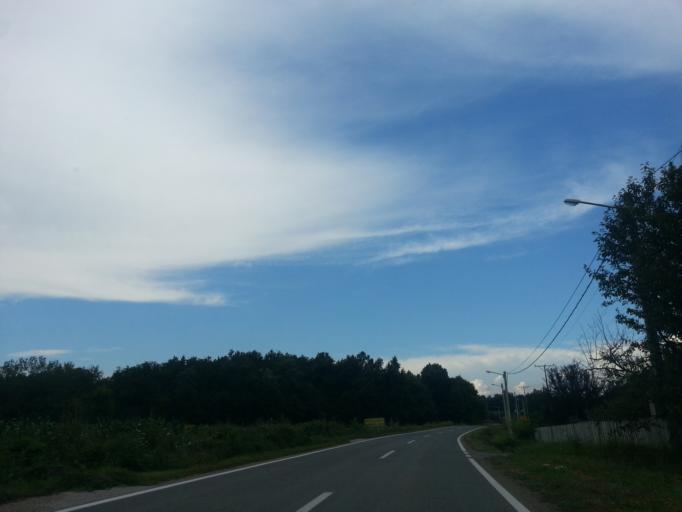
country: BA
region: Brcko
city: Brcko
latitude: 44.7923
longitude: 18.8160
